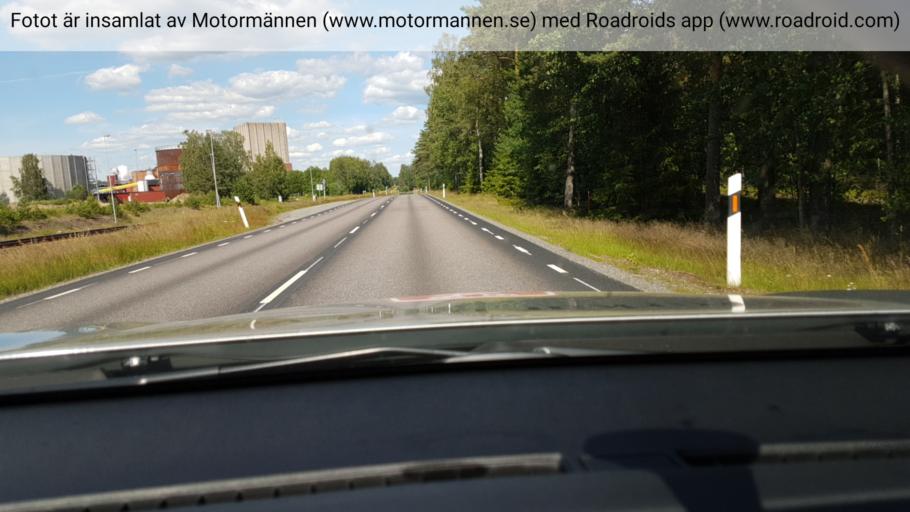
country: SE
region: Joenkoeping
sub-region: Vaggeryds Kommun
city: Vaggeryd
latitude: 57.4820
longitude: 14.1124
